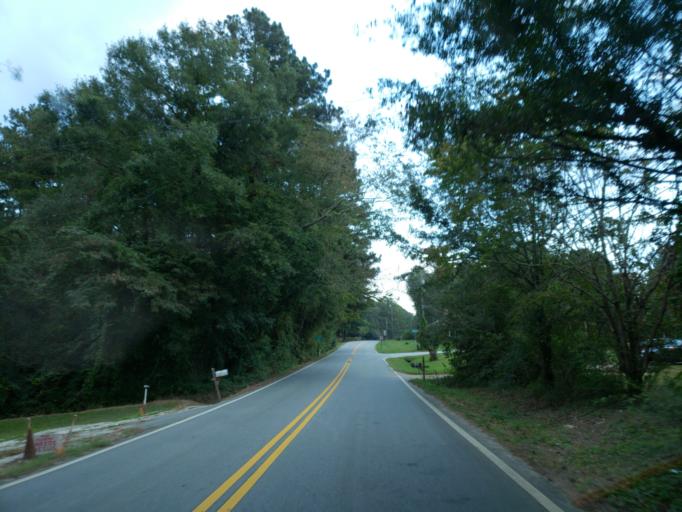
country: US
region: Georgia
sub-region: Cobb County
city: Powder Springs
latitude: 33.8436
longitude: -84.6937
